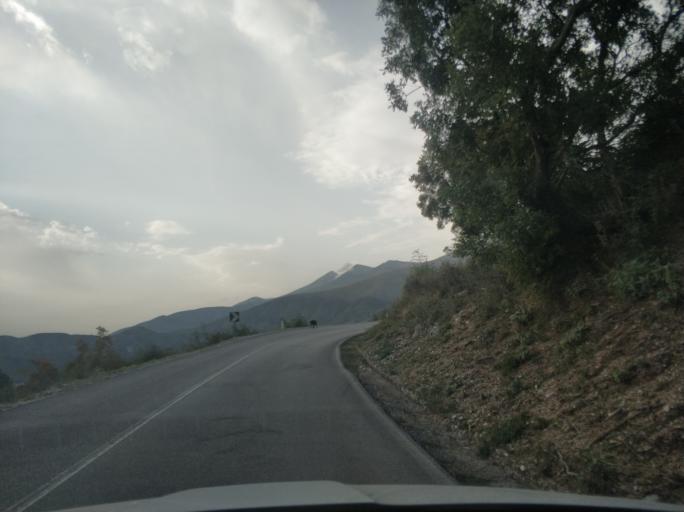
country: AL
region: Vlore
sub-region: Rrethi i Sarandes
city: Dhiver
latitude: 39.9235
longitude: 20.2028
